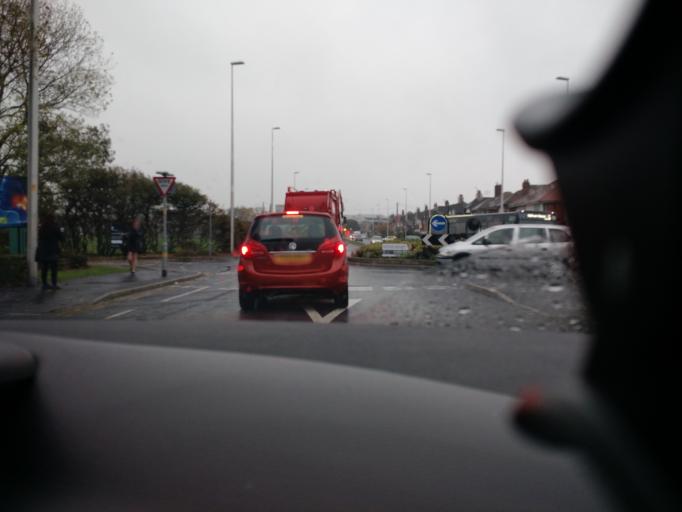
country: GB
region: England
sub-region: Lancashire
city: Great Marton
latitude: 53.8257
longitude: -3.0206
